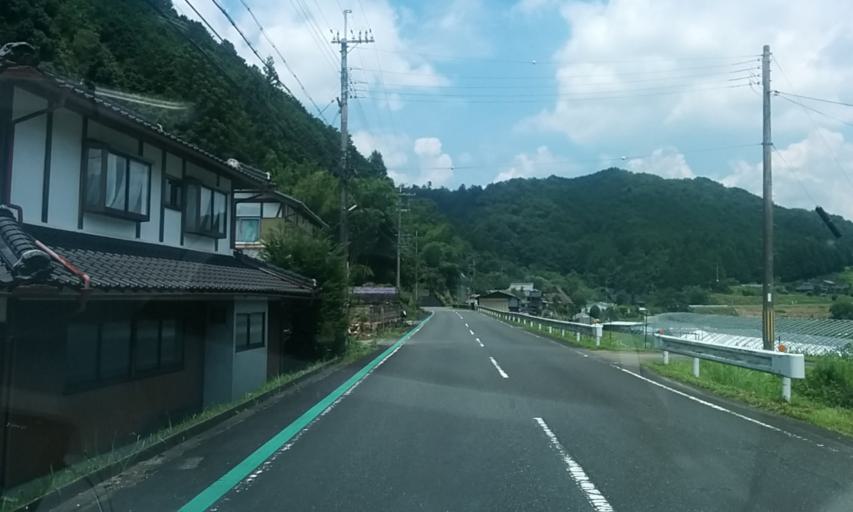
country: JP
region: Kyoto
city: Ayabe
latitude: 35.2074
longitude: 135.2264
